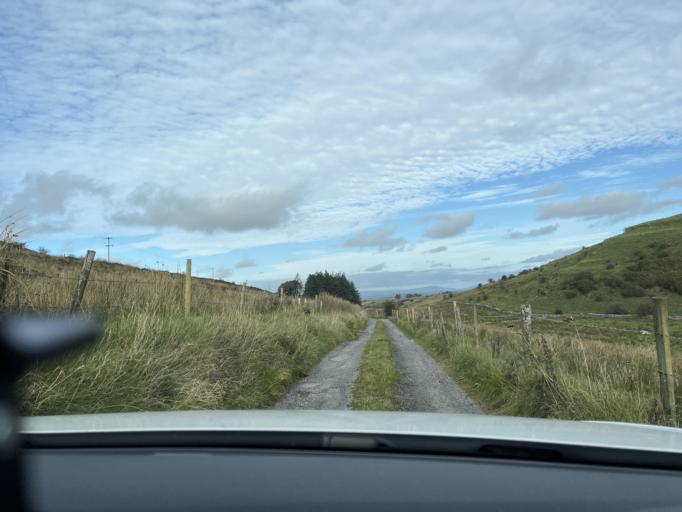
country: IE
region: Connaught
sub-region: Sligo
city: Ballymote
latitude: 54.0562
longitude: -8.4239
